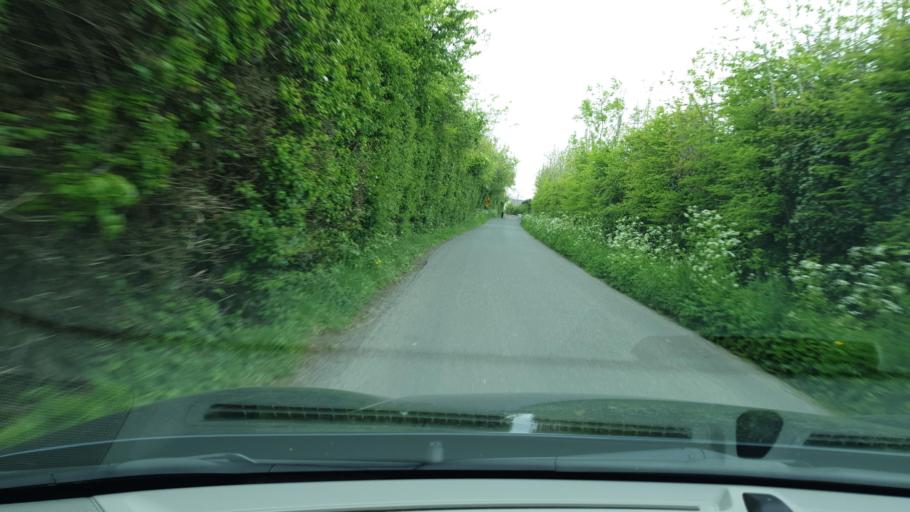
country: IE
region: Leinster
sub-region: An Mhi
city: Ratoath
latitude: 53.4882
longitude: -6.4991
